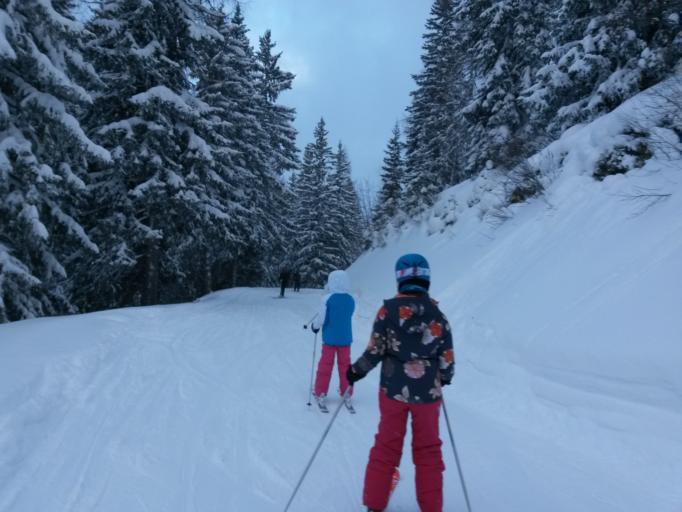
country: AT
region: Salzburg
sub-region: Politischer Bezirk Sankt Johann im Pongau
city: Dorfgastein
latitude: 47.2329
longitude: 13.1641
